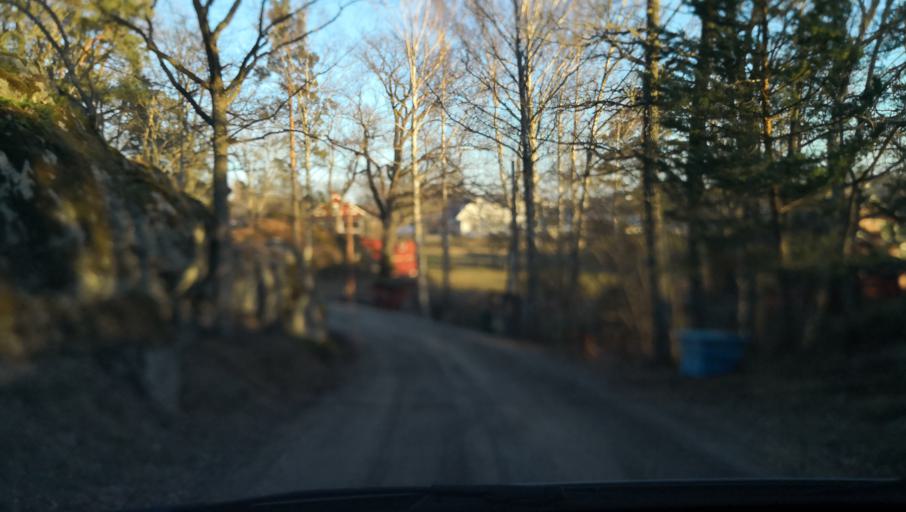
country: SE
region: Stockholm
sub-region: Varmdo Kommun
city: Mortnas
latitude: 59.3337
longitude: 18.4456
